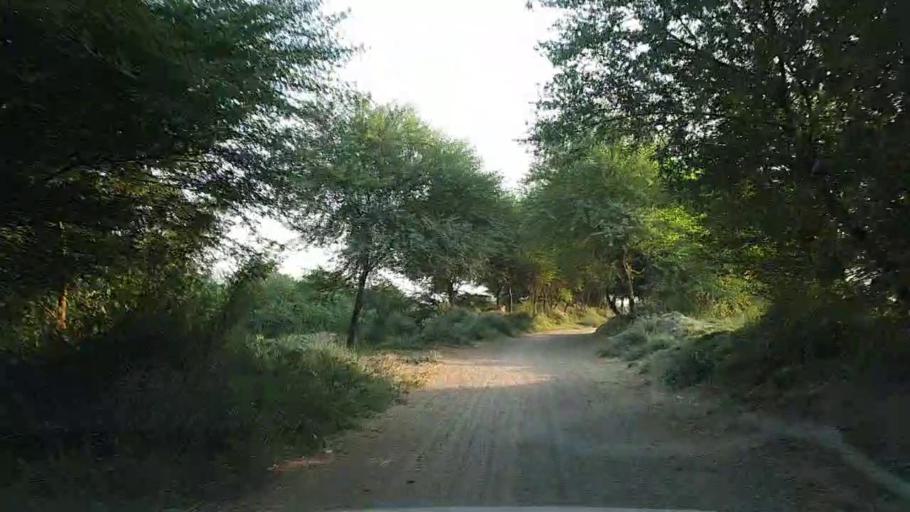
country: PK
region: Sindh
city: Daro Mehar
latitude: 24.7302
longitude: 68.1808
